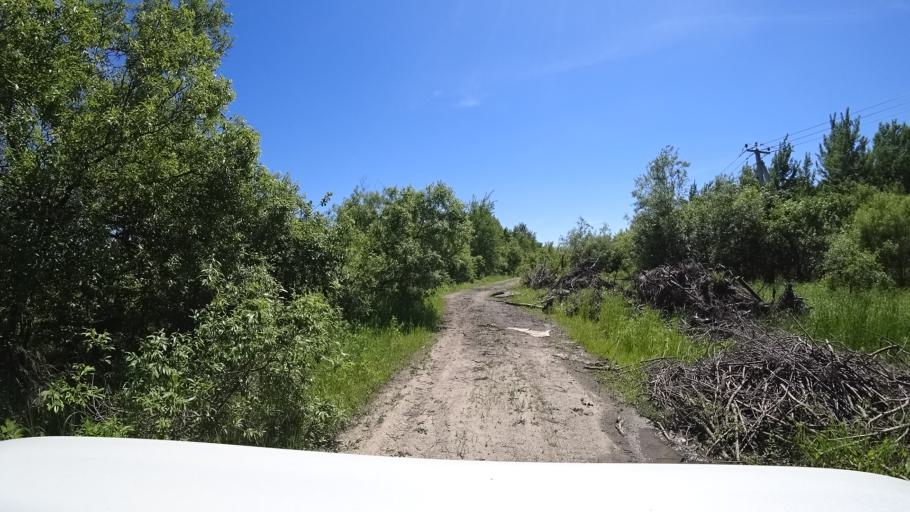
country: RU
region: Khabarovsk Krai
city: Topolevo
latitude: 48.4881
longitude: 135.1773
